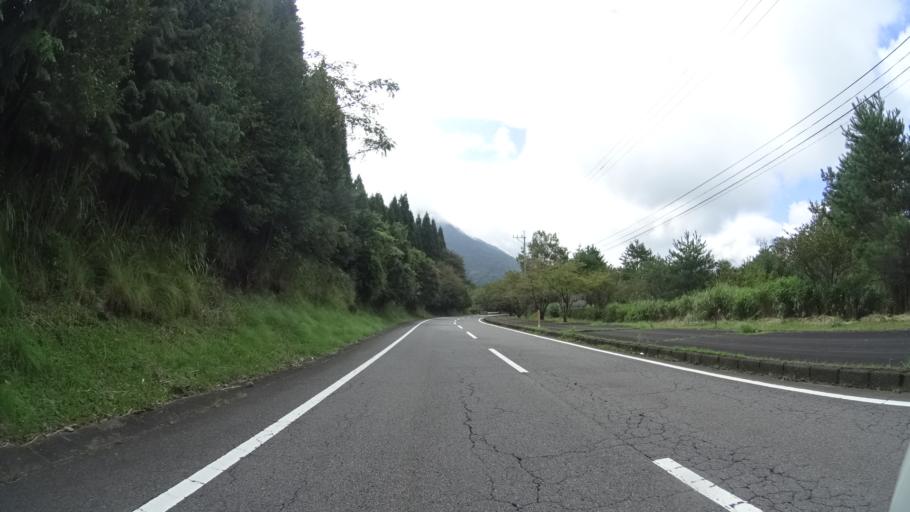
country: JP
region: Oita
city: Beppu
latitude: 33.3183
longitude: 131.4146
